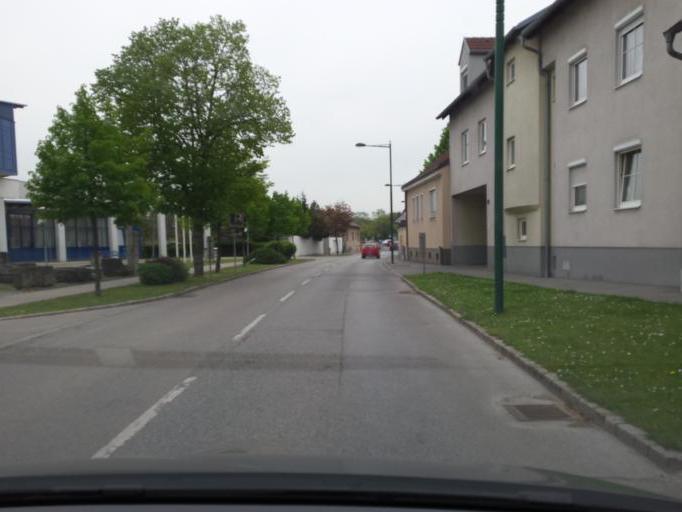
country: AT
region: Burgenland
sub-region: Politischer Bezirk Neusiedl am See
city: Bruckneudorf
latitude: 48.0289
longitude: 16.7781
